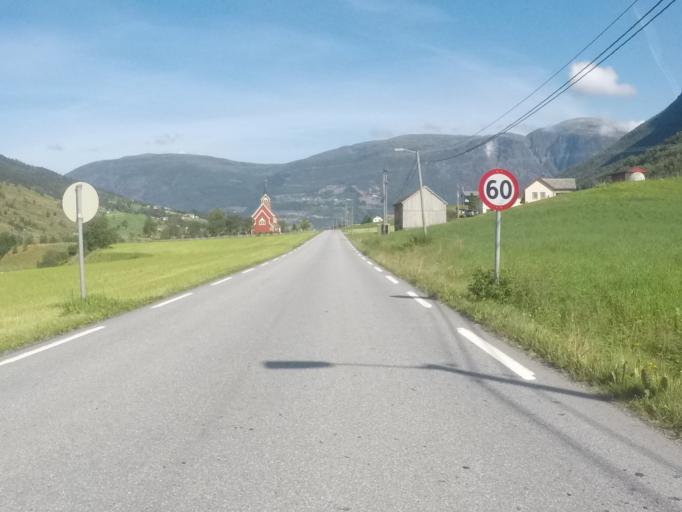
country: NO
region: Sogn og Fjordane
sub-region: Stryn
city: Stryn
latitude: 61.8249
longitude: 6.8093
